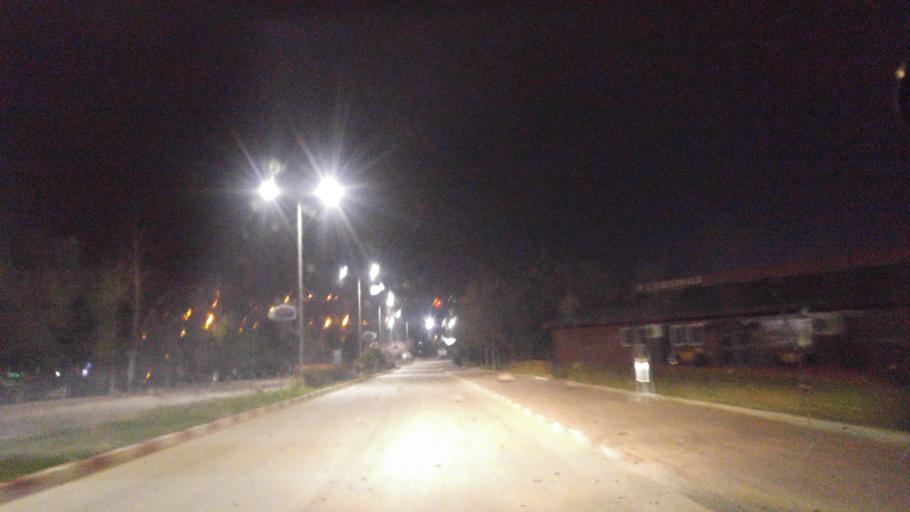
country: TR
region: Karabuk
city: Karabuk
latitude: 41.2119
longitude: 32.6542
